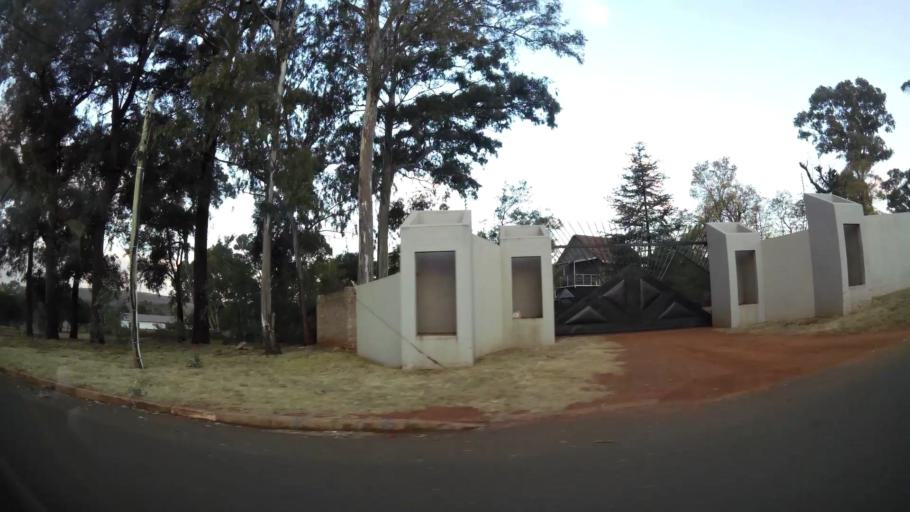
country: ZA
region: Gauteng
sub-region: West Rand District Municipality
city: Krugersdorp
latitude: -26.0676
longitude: 27.7942
